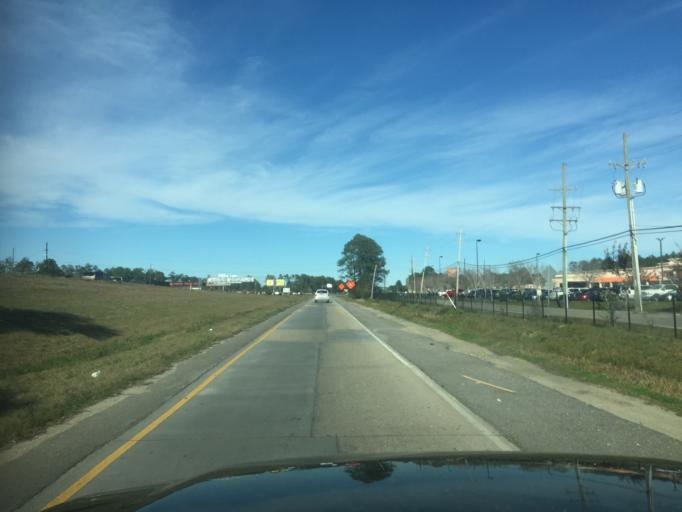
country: US
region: Louisiana
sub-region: Saint Tammany Parish
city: Slidell
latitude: 30.2859
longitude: -89.7486
